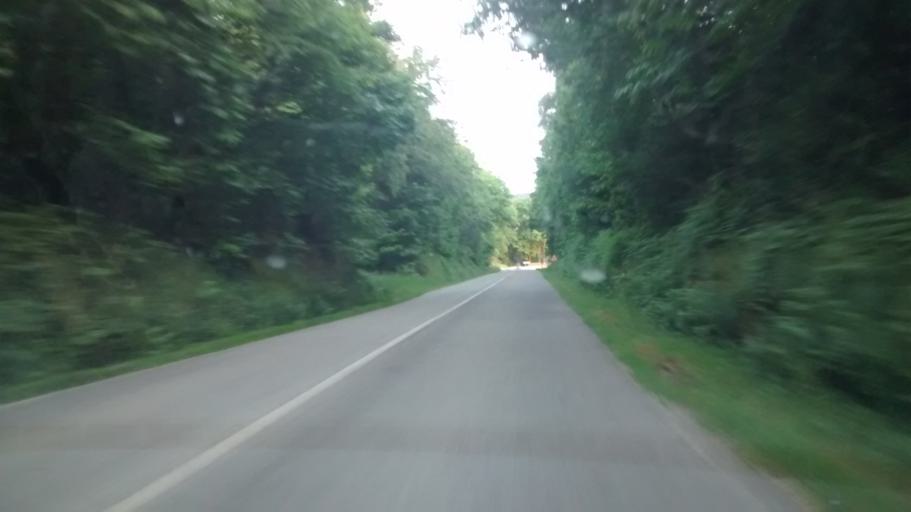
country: FR
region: Brittany
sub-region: Departement du Morbihan
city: Beignon
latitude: 47.9623
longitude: -2.1493
